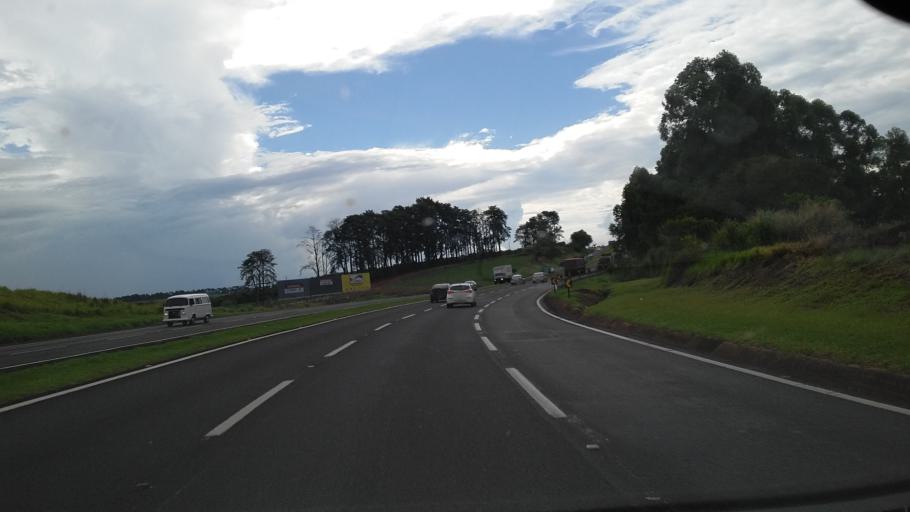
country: BR
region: Parana
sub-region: Rolandia
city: Rolandia
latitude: -23.3408
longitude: -51.3545
